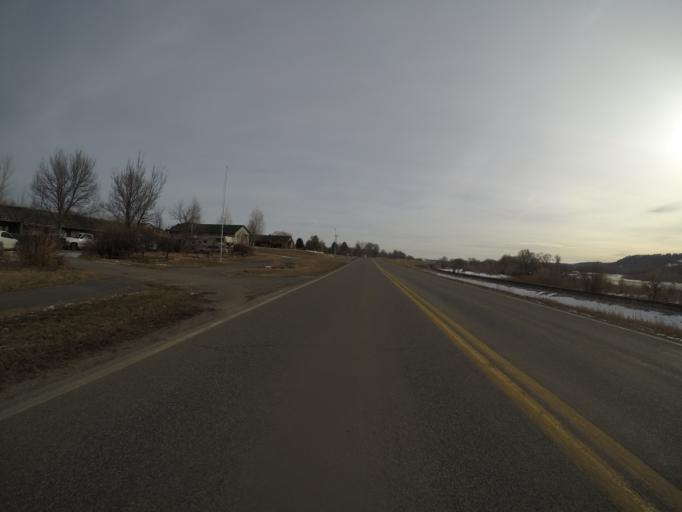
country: US
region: Montana
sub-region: Stillwater County
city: Columbus
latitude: 45.6406
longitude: -109.2680
